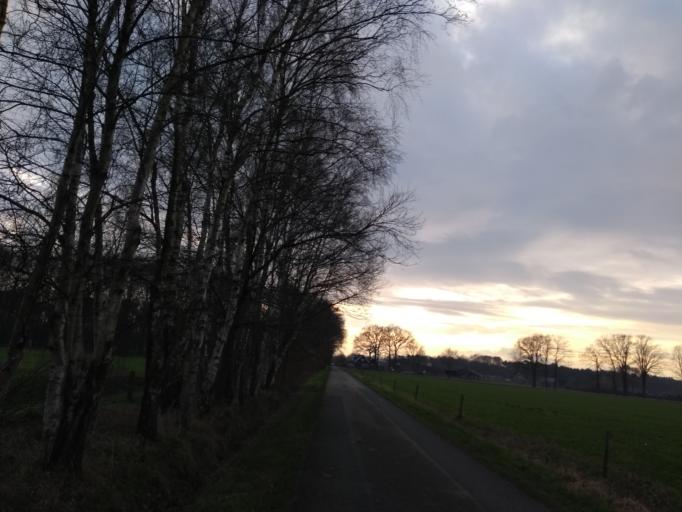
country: NL
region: Overijssel
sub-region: Gemeente Haaksbergen
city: Haaksbergen
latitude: 52.1298
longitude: 6.7592
